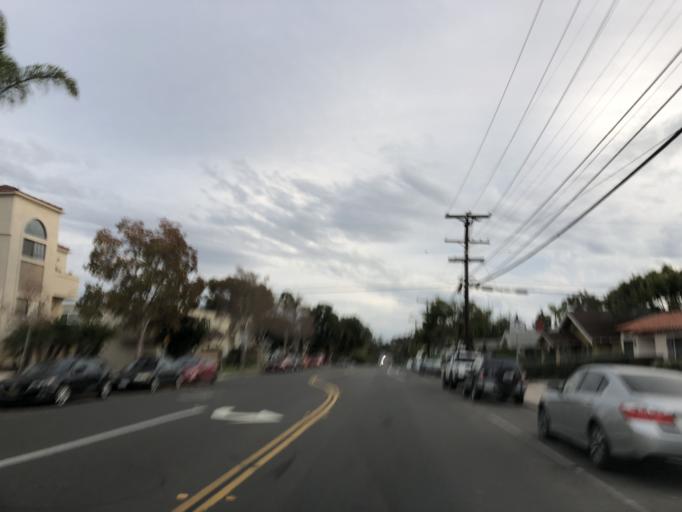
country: US
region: California
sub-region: San Diego County
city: San Diego
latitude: 32.7461
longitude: -117.1513
